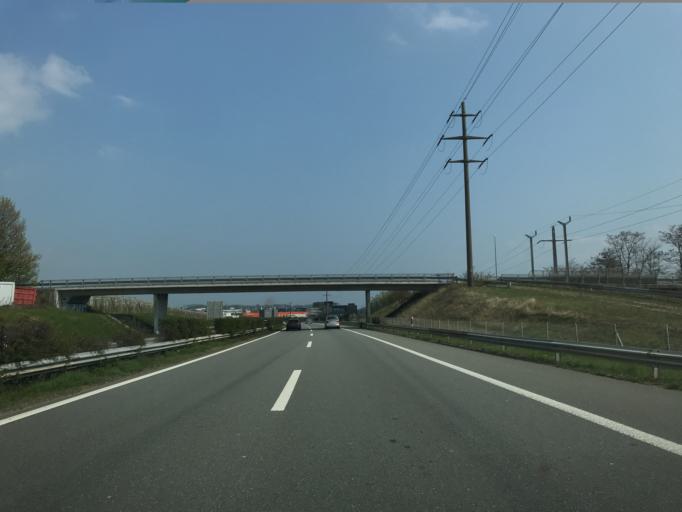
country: CH
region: Vaud
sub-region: Morges District
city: Aubonne
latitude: 46.4769
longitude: 6.4131
